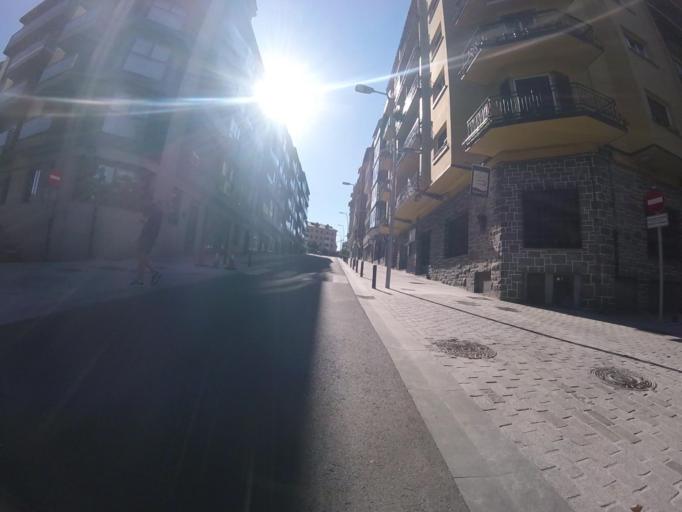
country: ES
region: Basque Country
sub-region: Provincia de Guipuzcoa
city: Irun
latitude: 43.3382
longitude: -1.7876
